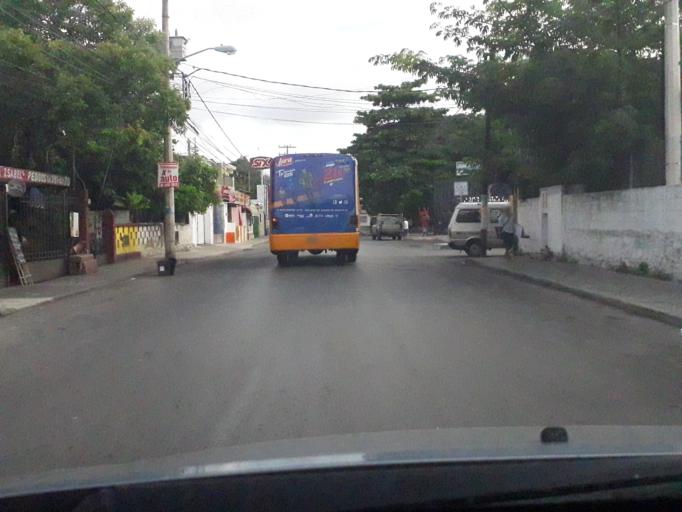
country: MX
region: Yucatan
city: Merida
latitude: 21.0133
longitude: -89.6322
